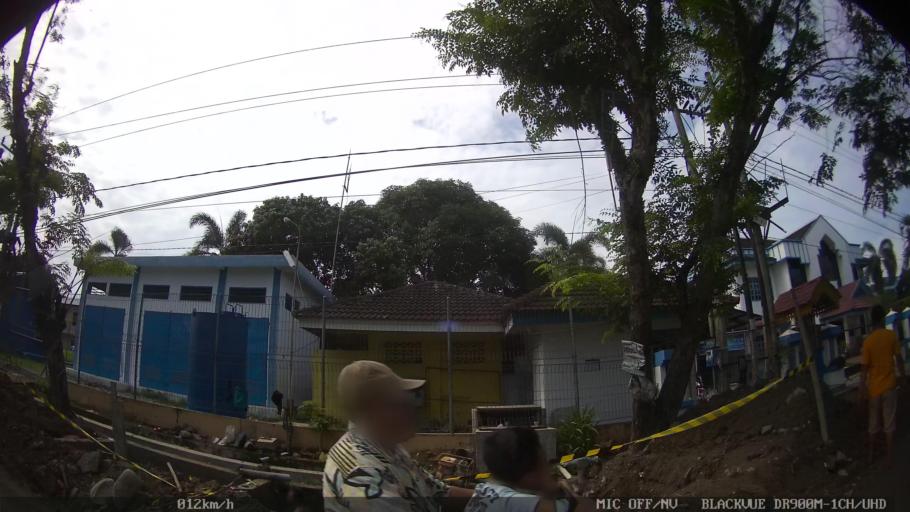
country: ID
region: North Sumatra
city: Medan
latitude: 3.5864
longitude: 98.7320
